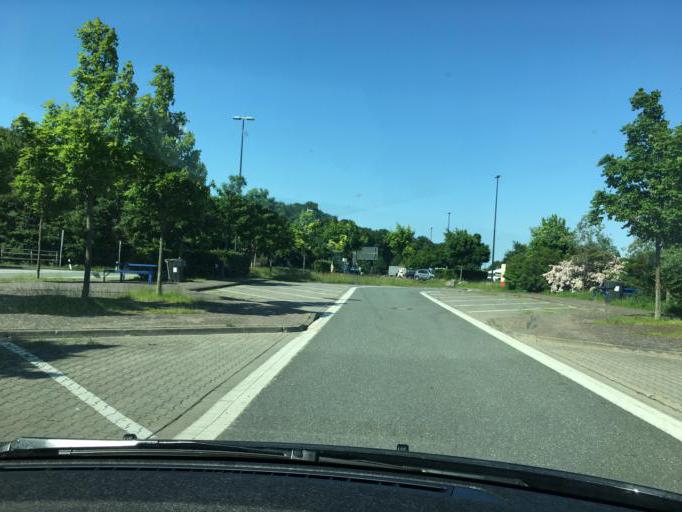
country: DE
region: North Rhine-Westphalia
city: Lengerich
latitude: 52.2304
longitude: 7.8764
